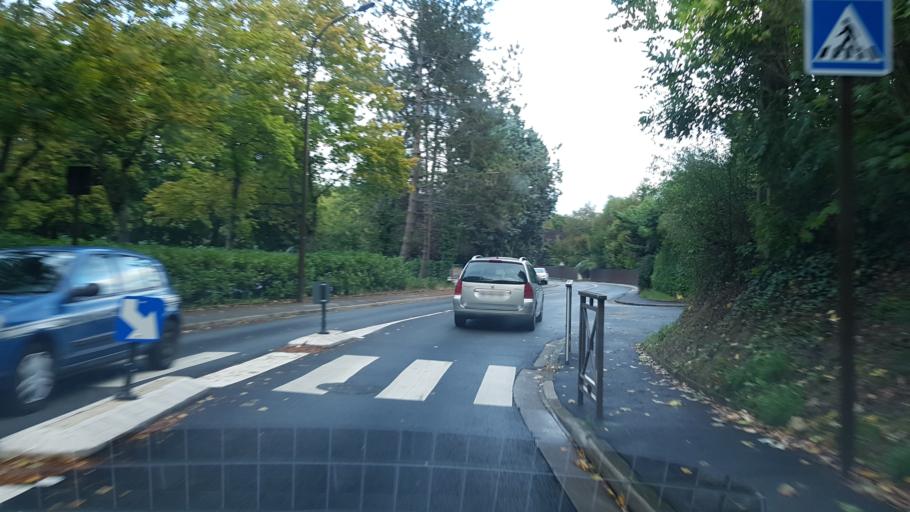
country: FR
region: Ile-de-France
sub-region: Departement de l'Essonne
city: Gif-sur-Yvette
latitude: 48.6962
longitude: 2.1298
